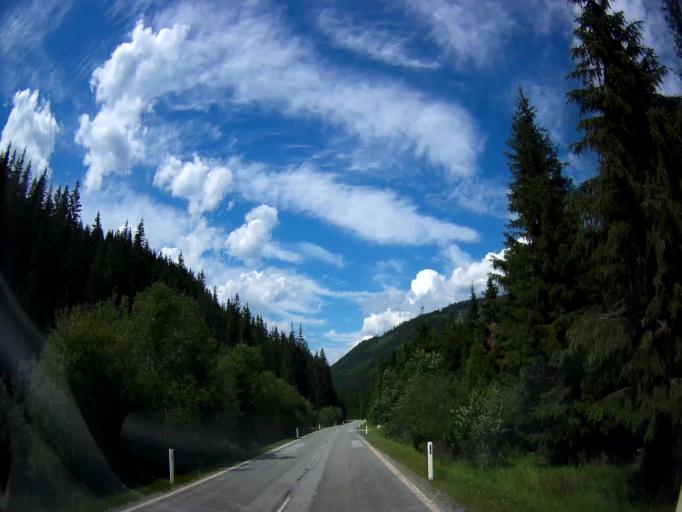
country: AT
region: Styria
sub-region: Politischer Bezirk Murau
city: Stadl an der Mur
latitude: 46.9946
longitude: 14.0151
